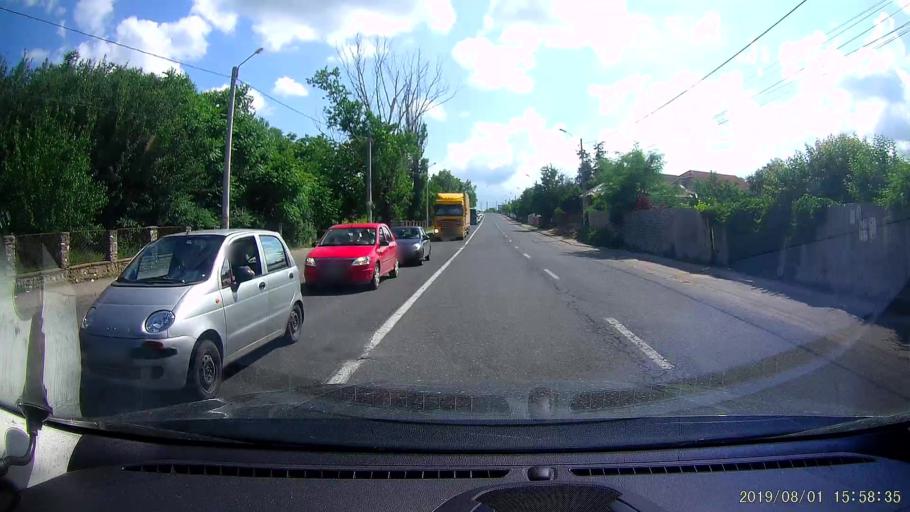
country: RO
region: Ialomita
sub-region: Comuna Slobozia
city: Slobozia
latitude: 44.5618
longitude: 27.3832
